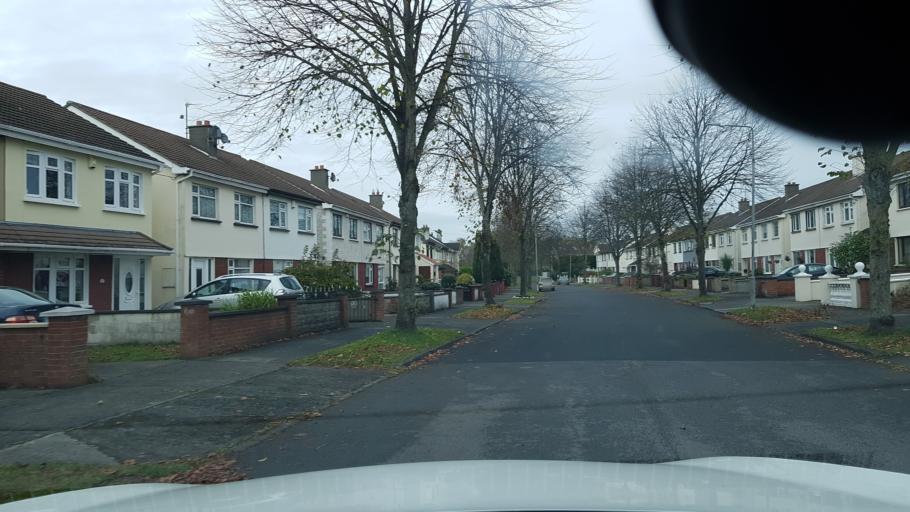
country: IE
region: Leinster
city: Hartstown
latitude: 53.3927
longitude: -6.4162
